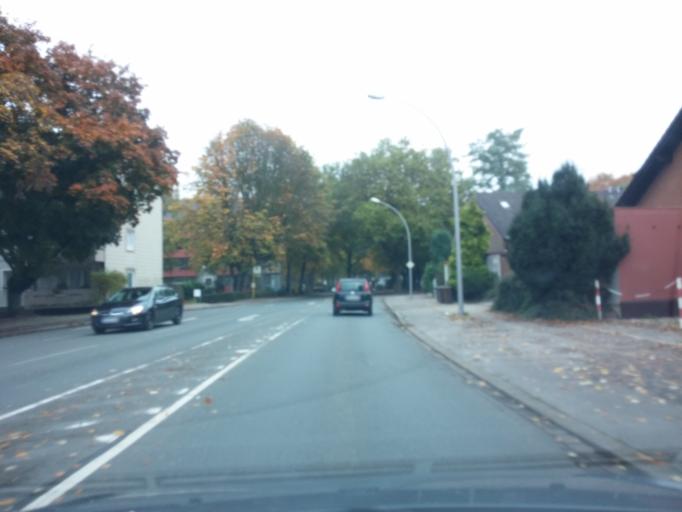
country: DE
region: North Rhine-Westphalia
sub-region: Regierungsbezirk Munster
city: Gladbeck
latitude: 51.5823
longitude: 7.0030
